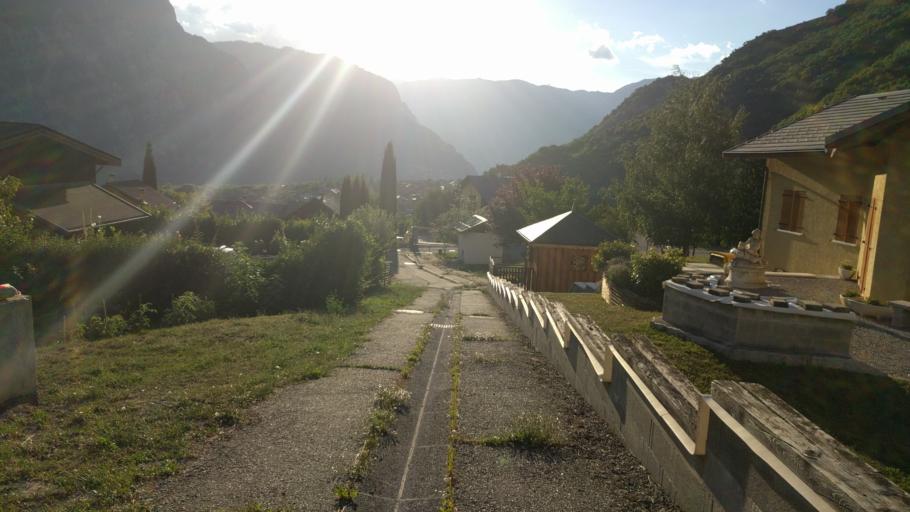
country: FR
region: Rhone-Alpes
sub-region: Departement de la Savoie
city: Villargondran
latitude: 45.2555
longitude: 6.4169
